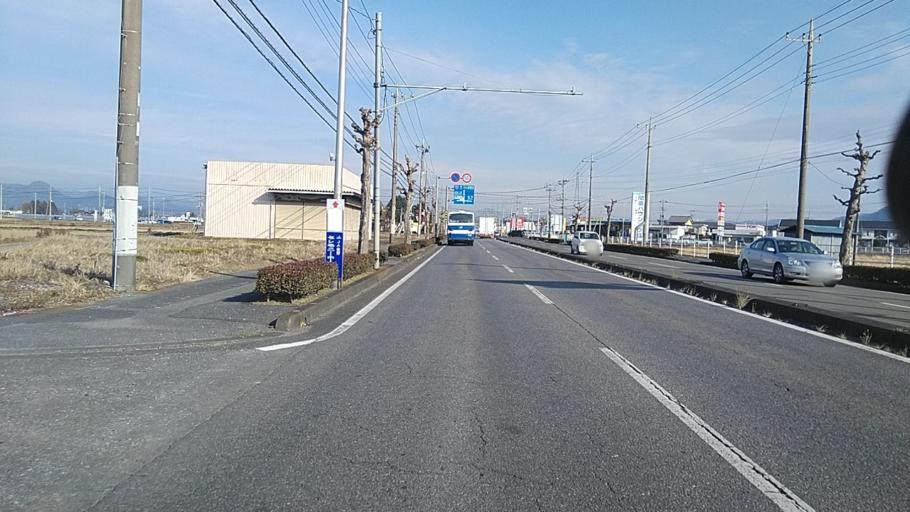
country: JP
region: Tochigi
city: Sano
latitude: 36.3404
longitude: 139.5717
